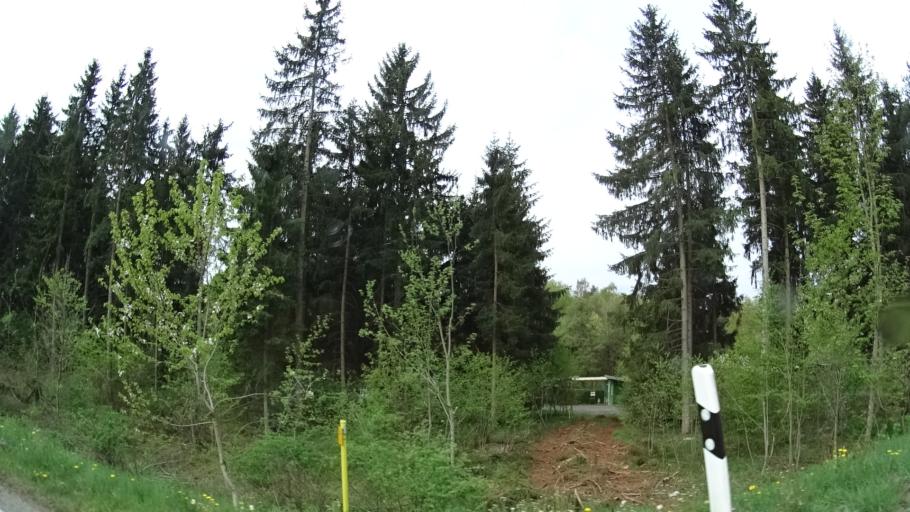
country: DE
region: Baden-Wuerttemberg
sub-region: Freiburg Region
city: Monchweiler
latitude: 48.0843
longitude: 8.4529
